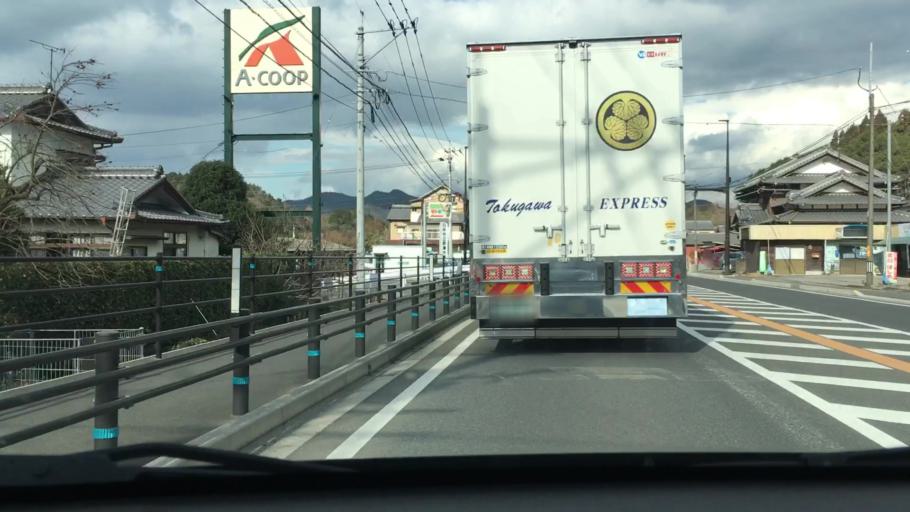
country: JP
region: Oita
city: Usuki
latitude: 33.0373
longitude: 131.6895
